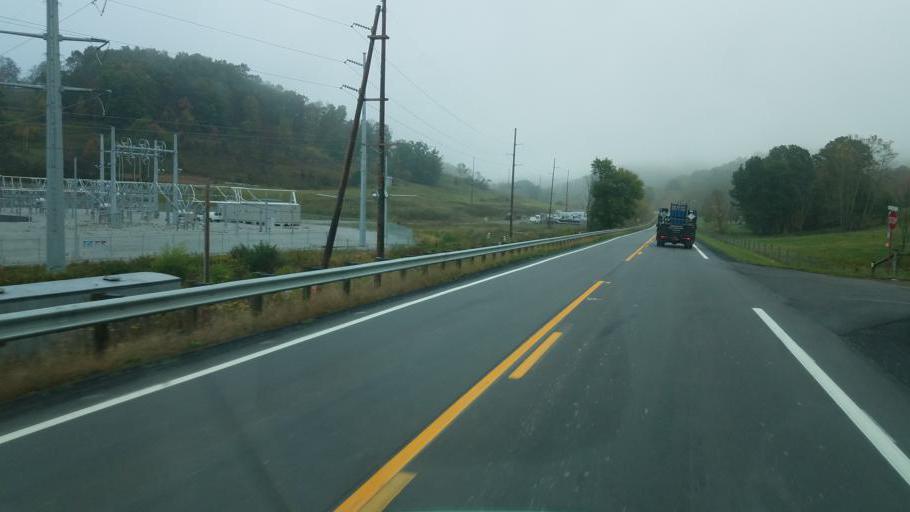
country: US
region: Ohio
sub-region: Tuscarawas County
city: Dennison
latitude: 40.4028
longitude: -81.2417
